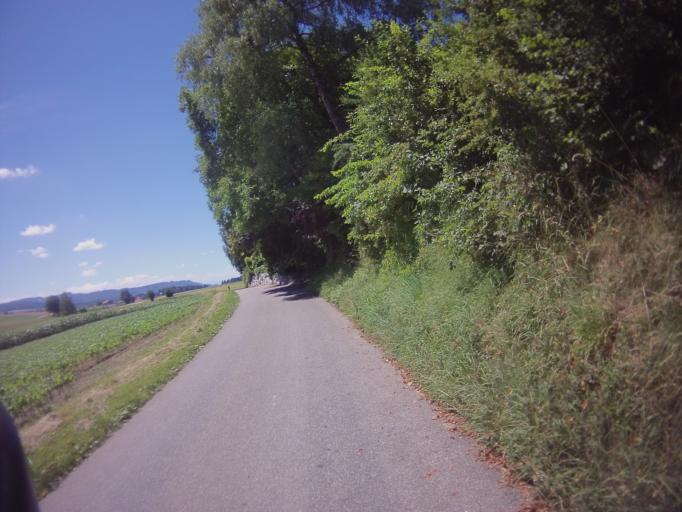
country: CH
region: Bern
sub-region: Bern-Mittelland District
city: Fraubrunnen
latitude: 47.0698
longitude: 7.5393
